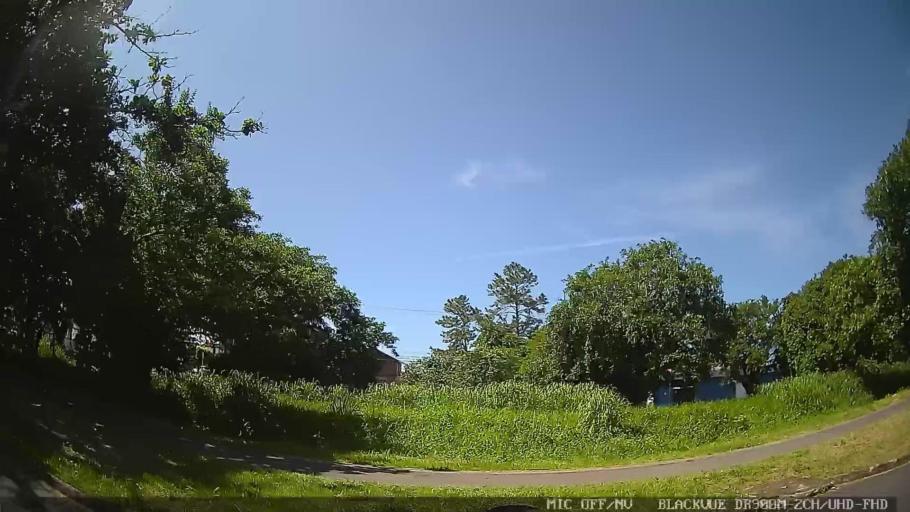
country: BR
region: Sao Paulo
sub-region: Peruibe
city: Peruibe
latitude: -24.3158
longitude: -47.0036
